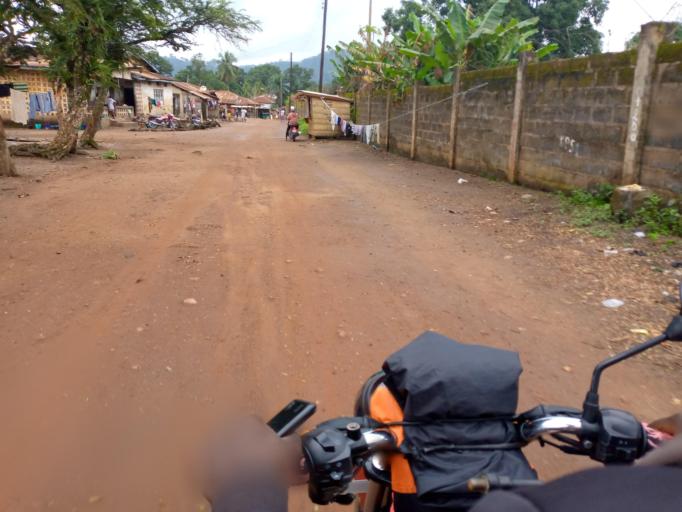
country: SL
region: Eastern Province
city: Kenema
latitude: 7.8734
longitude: -11.1858
